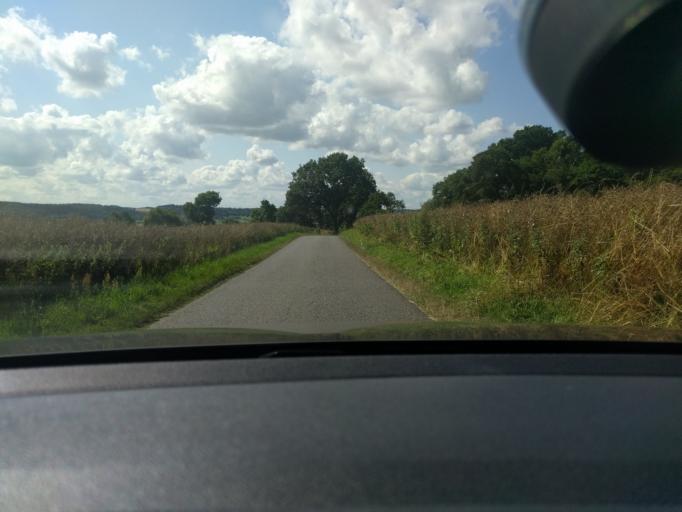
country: DK
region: Central Jutland
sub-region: Viborg Kommune
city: Bjerringbro
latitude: 56.4607
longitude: 9.5919
